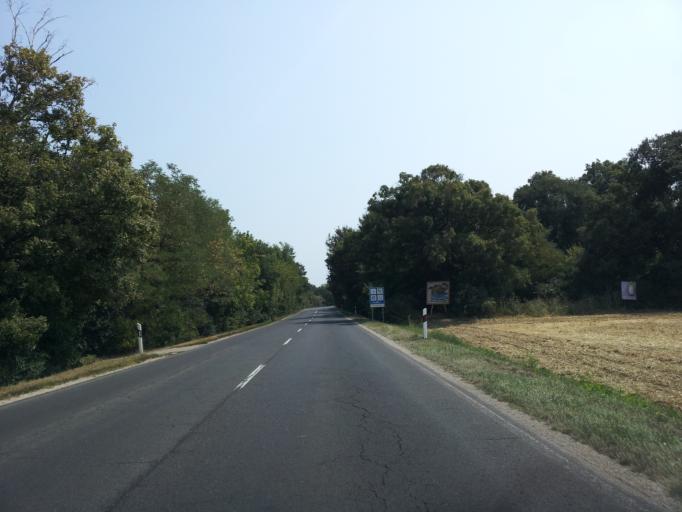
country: HU
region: Veszprem
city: Csopak
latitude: 47.0204
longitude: 17.9111
